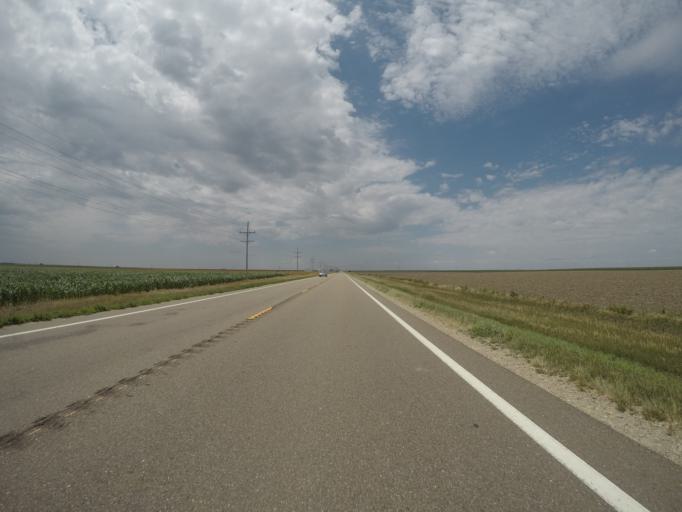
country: US
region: Kansas
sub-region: Thomas County
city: Colby
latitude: 39.3943
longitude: -100.8926
